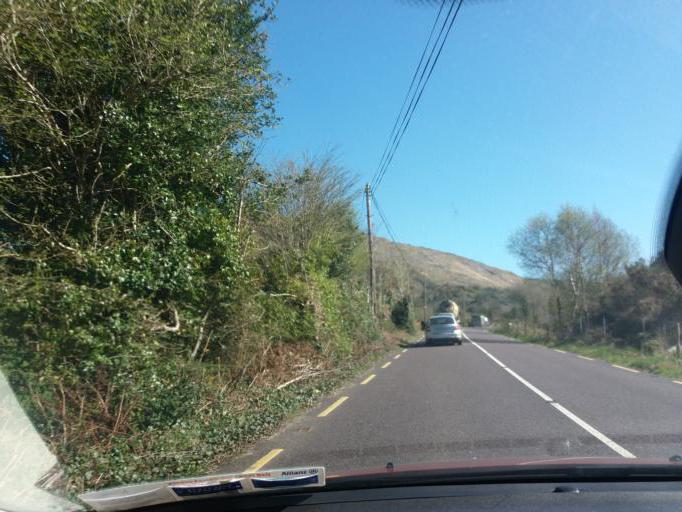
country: IE
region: Munster
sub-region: Ciarrai
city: Cill Airne
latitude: 51.9791
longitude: -9.3265
